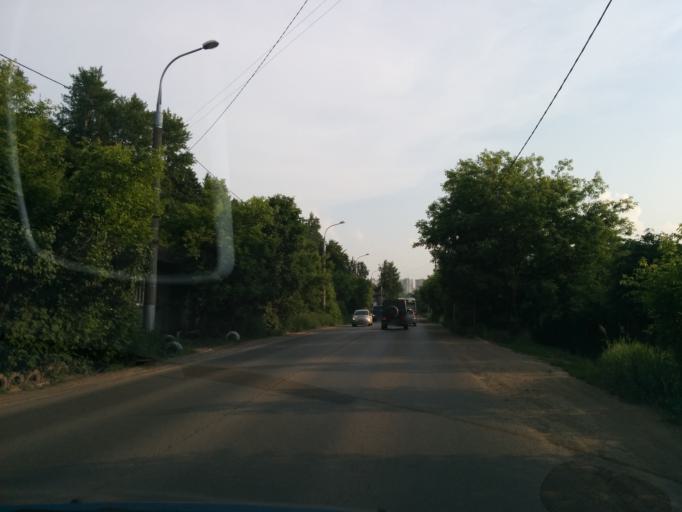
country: RU
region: Perm
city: Perm
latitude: 58.0444
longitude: 56.3207
